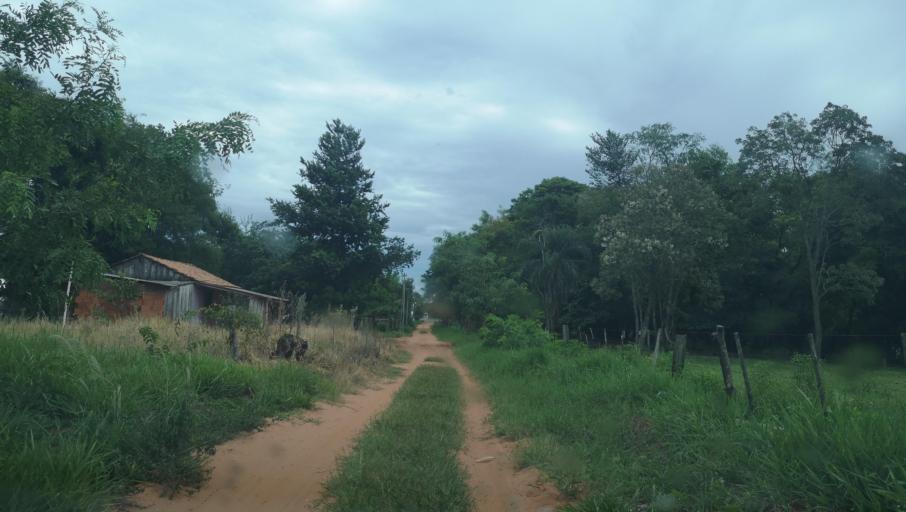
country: PY
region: San Pedro
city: Capiibary
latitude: -24.7422
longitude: -56.0220
